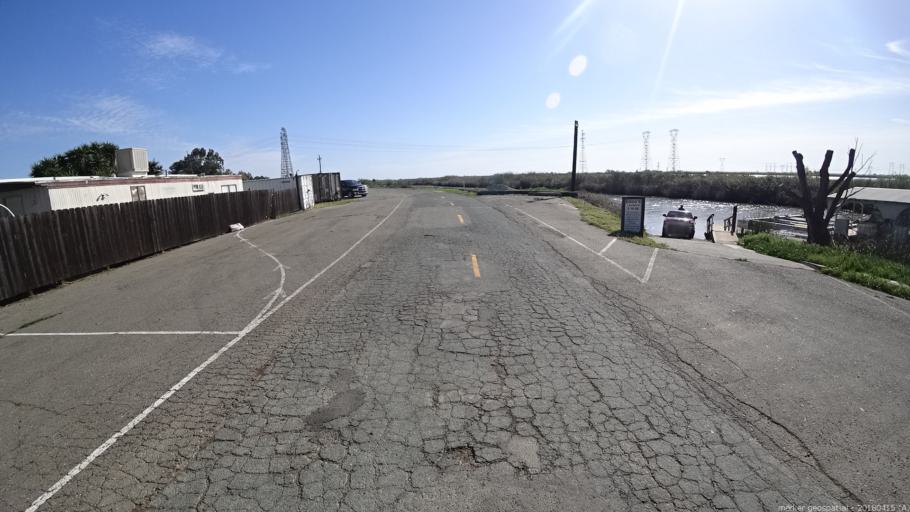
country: US
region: California
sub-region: Contra Costa County
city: Oakley
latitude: 38.0508
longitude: -121.6998
